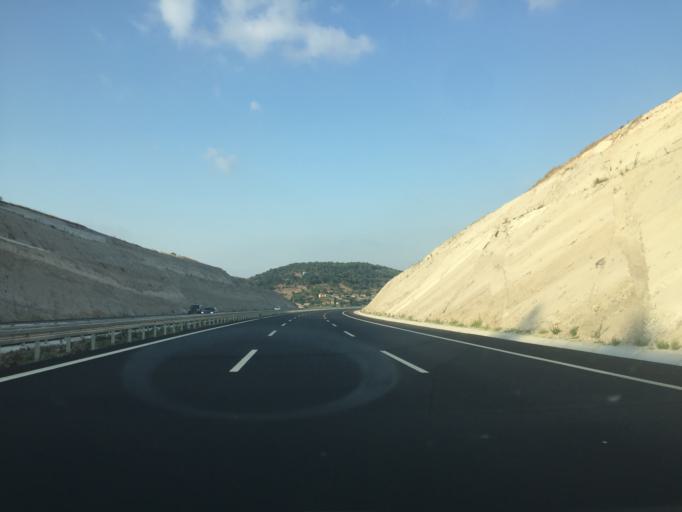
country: TR
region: Balikesir
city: Ertugrul
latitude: 39.5456
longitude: 27.6797
